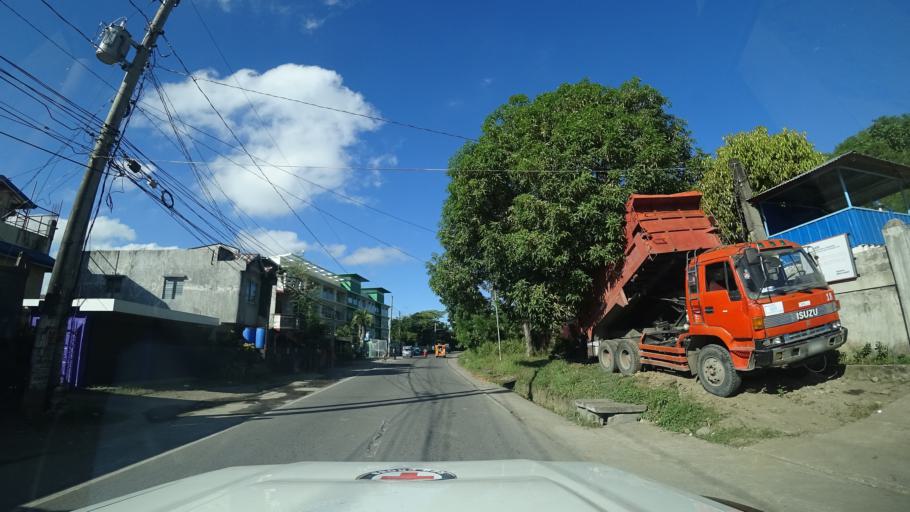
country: PH
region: Eastern Visayas
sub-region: Province of Leyte
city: Panalanoy
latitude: 11.2313
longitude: 124.9997
